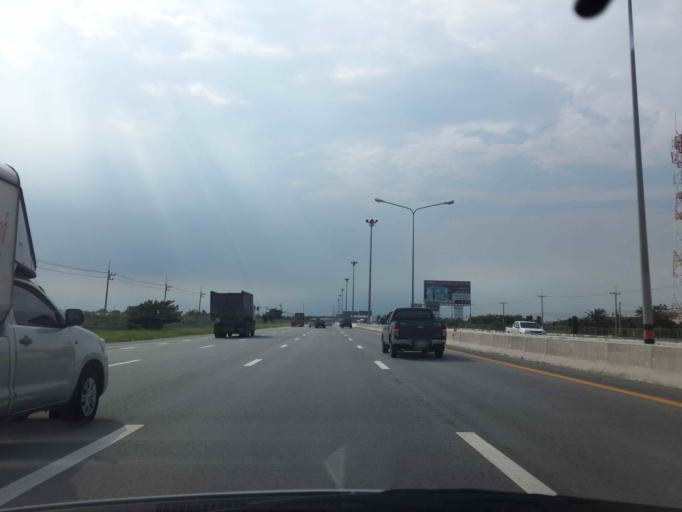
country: TH
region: Chachoengsao
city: Bang Pakong
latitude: 13.6041
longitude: 100.9463
